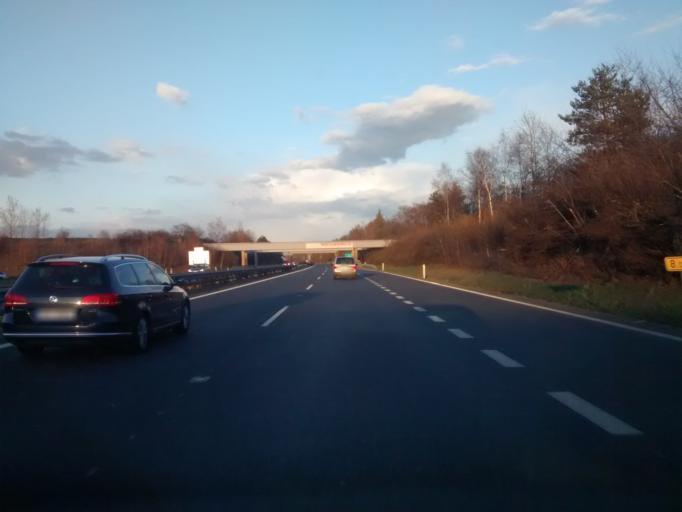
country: CZ
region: Central Bohemia
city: Jirny
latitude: 50.1225
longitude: 14.7056
